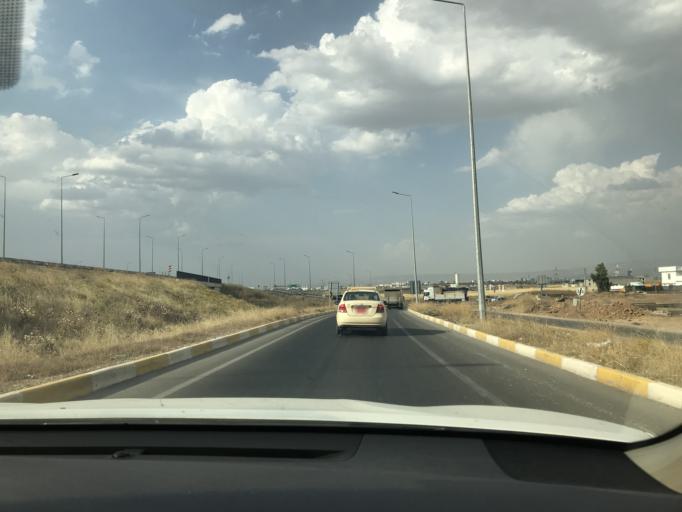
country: IQ
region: Arbil
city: Erbil
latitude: 36.2077
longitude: 43.9540
